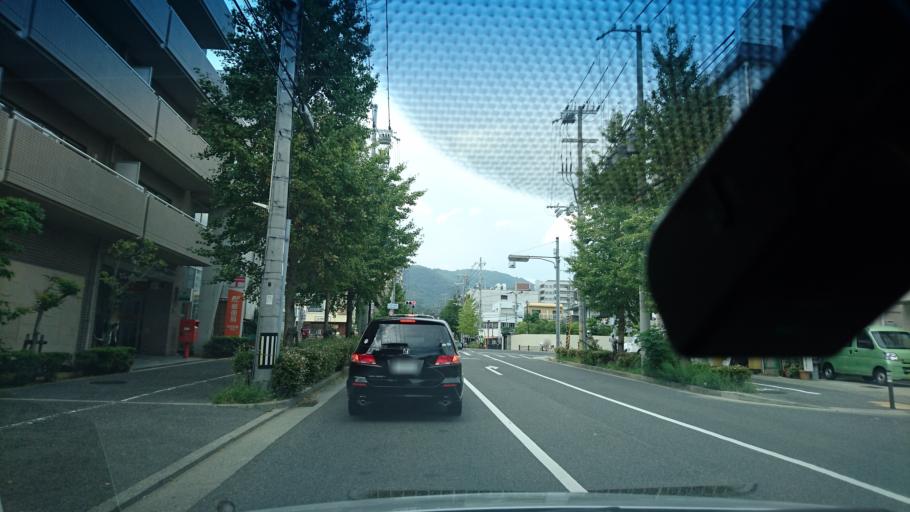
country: JP
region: Hyogo
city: Ashiya
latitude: 34.7325
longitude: 135.3094
